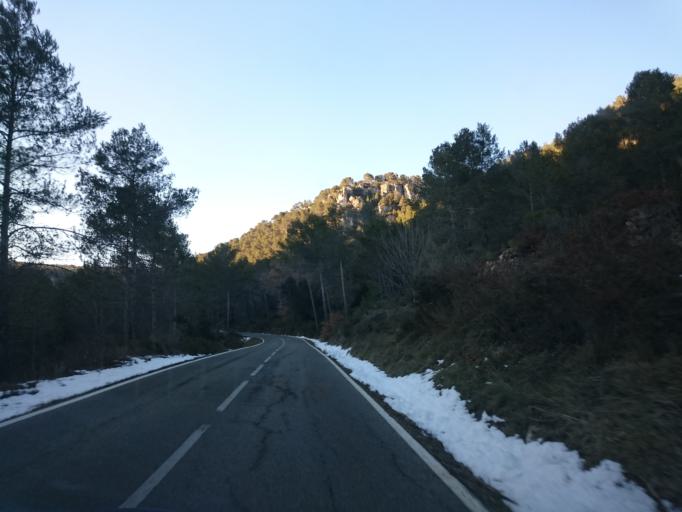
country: ES
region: Catalonia
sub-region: Provincia de Tarragona
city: Querol
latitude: 41.3786
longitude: 1.4775
